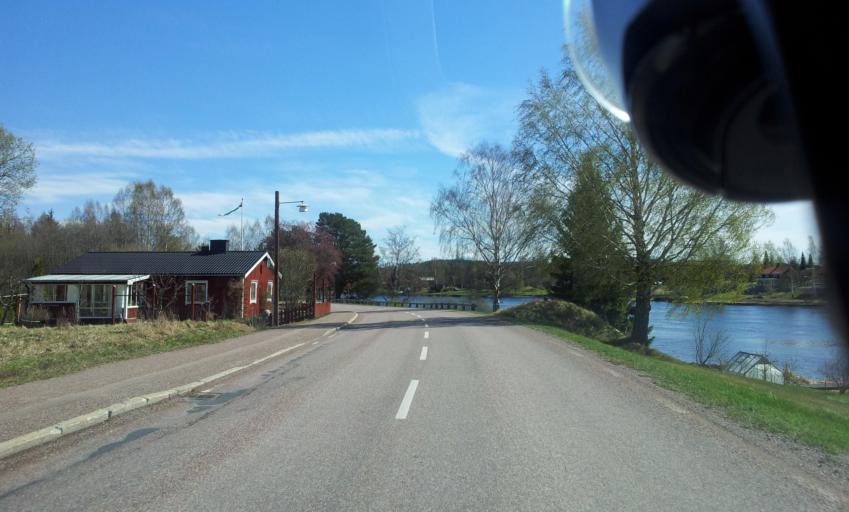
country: SE
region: Dalarna
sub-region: Borlange Kommun
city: Ornas
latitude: 60.4621
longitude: 15.5465
